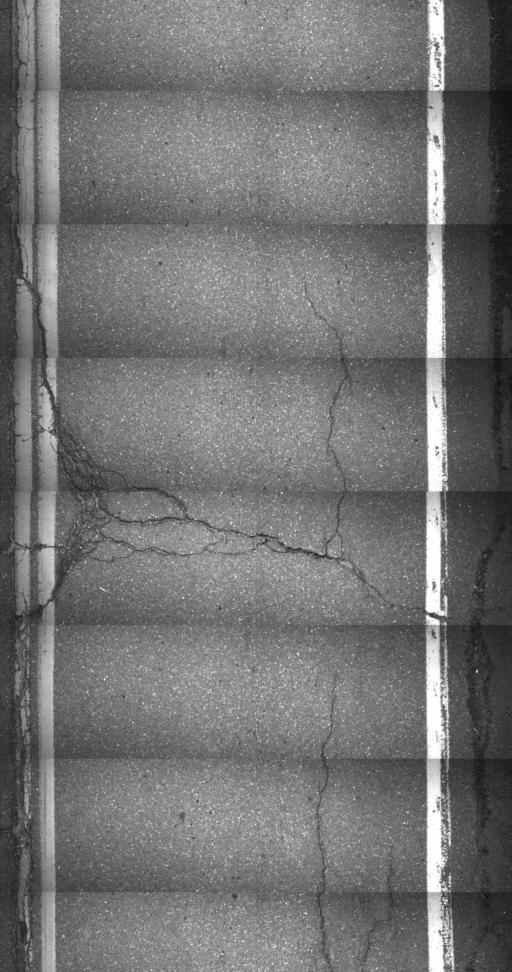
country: US
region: New Hampshire
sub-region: Grafton County
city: Woodsville
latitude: 44.2172
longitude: -72.0589
